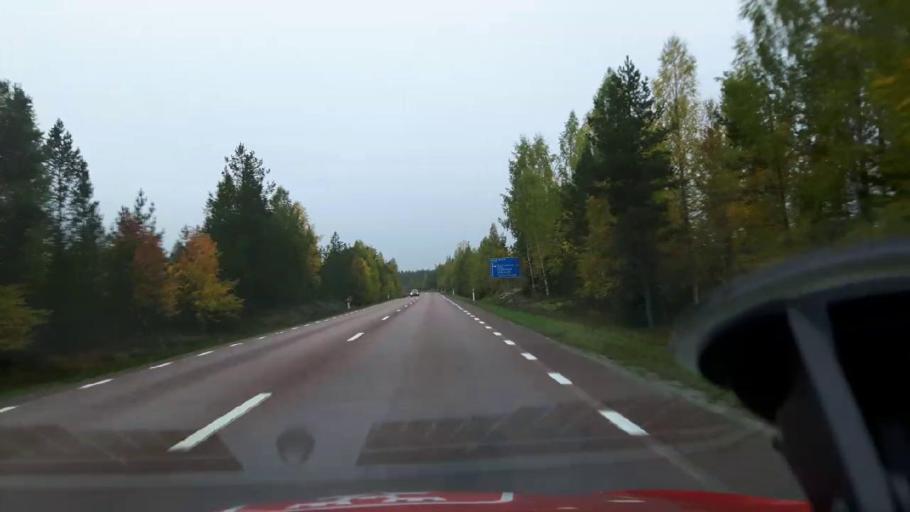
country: SE
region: Jaemtland
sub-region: Bergs Kommun
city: Hoverberg
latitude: 62.6250
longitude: 14.3714
